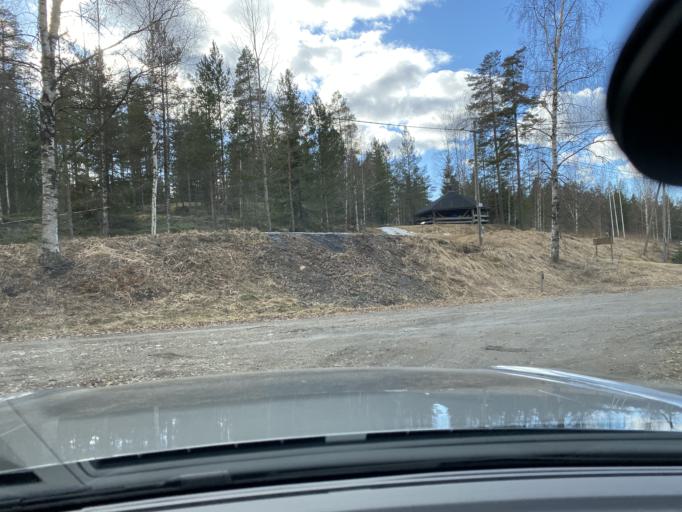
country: FI
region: Pirkanmaa
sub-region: Lounais-Pirkanmaa
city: Punkalaidun
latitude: 61.0917
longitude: 23.1368
